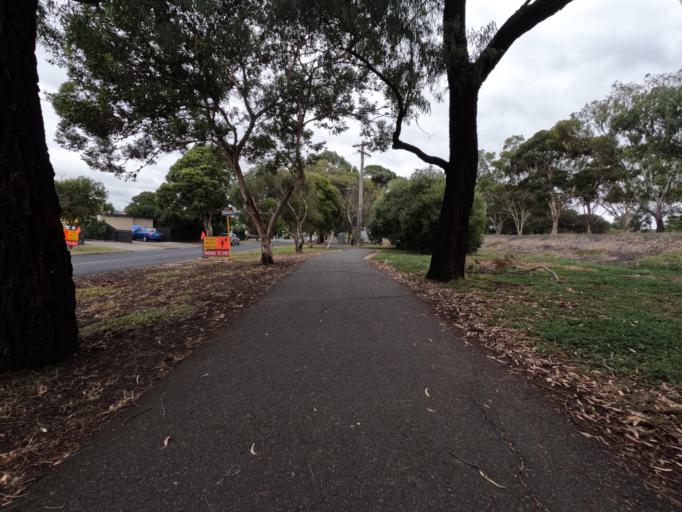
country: AU
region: Victoria
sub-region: Greater Geelong
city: Hamlyn Heights
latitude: -38.1319
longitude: 144.3231
